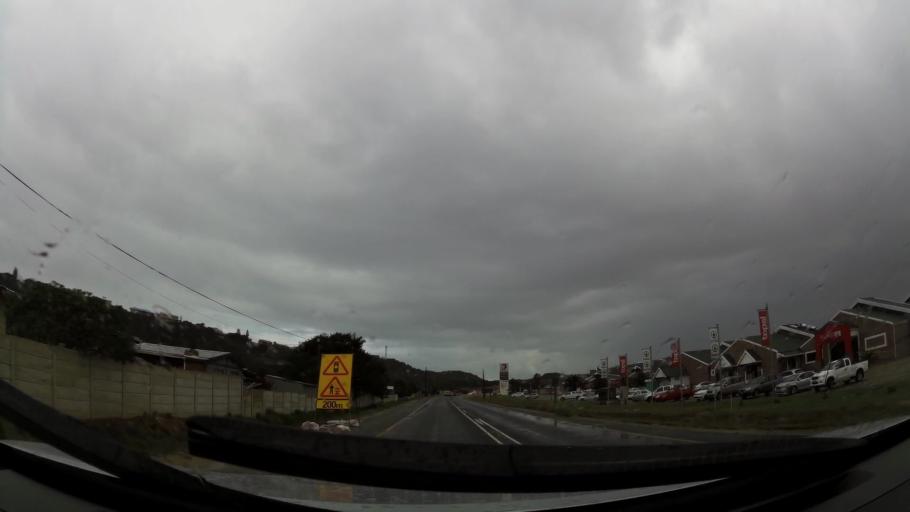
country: ZA
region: Western Cape
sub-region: Eden District Municipality
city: Mossel Bay
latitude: -34.0539
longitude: 22.2265
